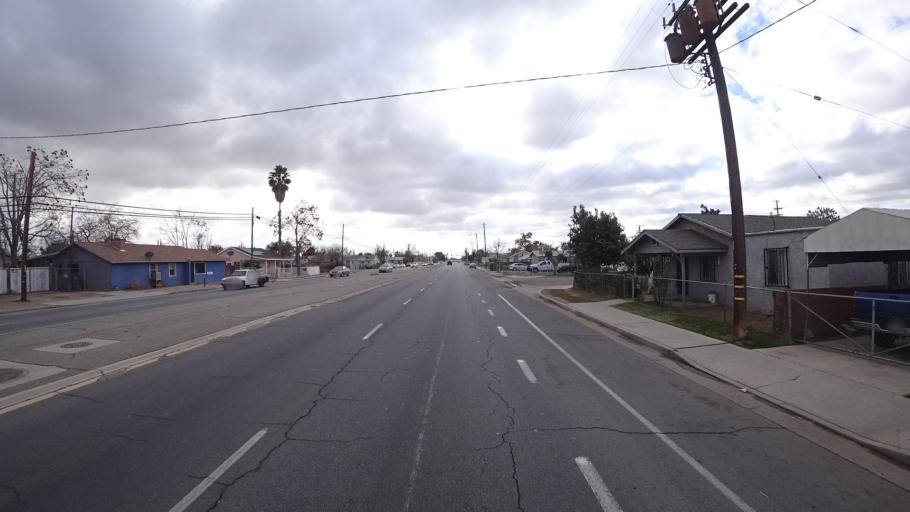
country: US
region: California
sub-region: Kern County
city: Bakersfield
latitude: 35.3675
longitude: -118.9676
